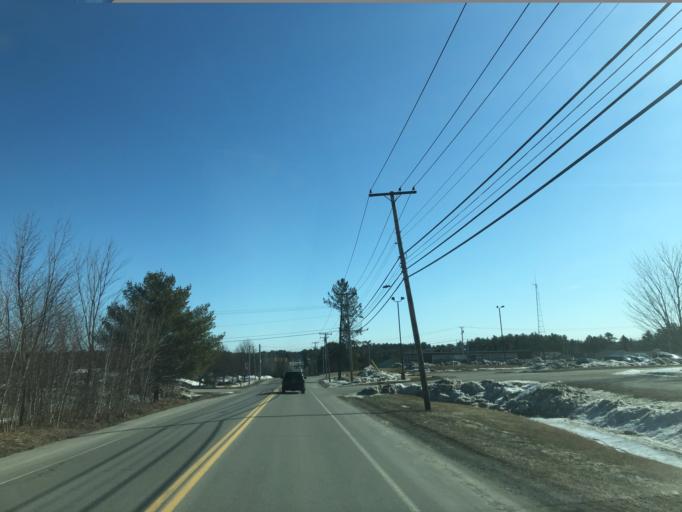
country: US
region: Maine
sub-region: Penobscot County
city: Brewer
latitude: 44.8218
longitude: -68.7420
